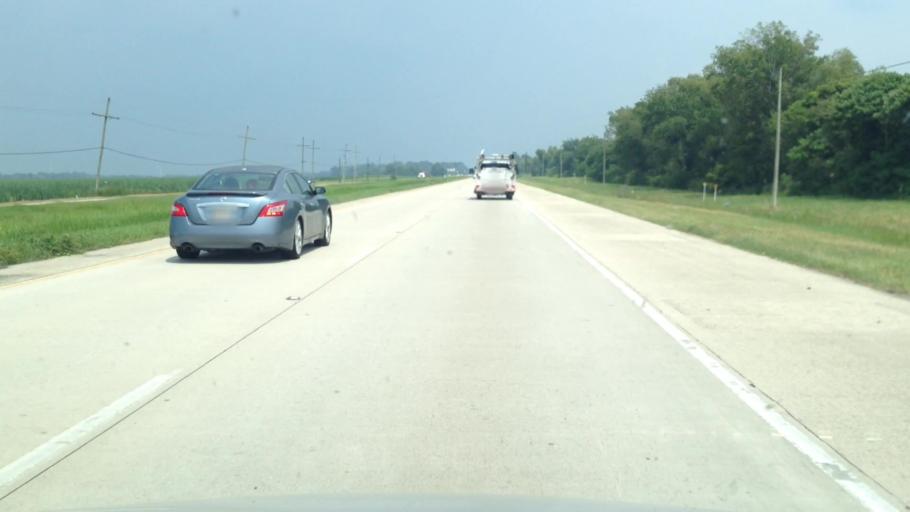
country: US
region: Louisiana
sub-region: West Baton Rouge Parish
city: Port Allen
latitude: 30.4947
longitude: -91.2940
